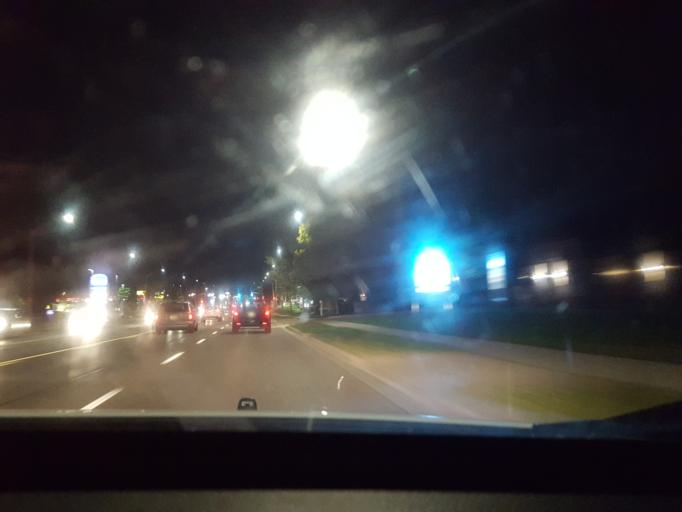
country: CA
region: Ontario
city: Hamilton
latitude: 43.2137
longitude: -79.8882
